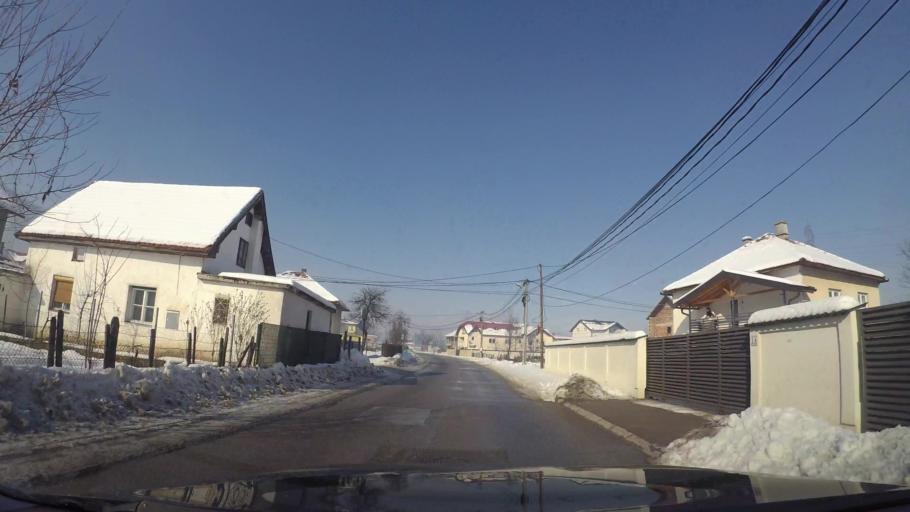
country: BA
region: Federation of Bosnia and Herzegovina
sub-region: Kanton Sarajevo
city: Sarajevo
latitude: 43.8073
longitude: 18.3005
